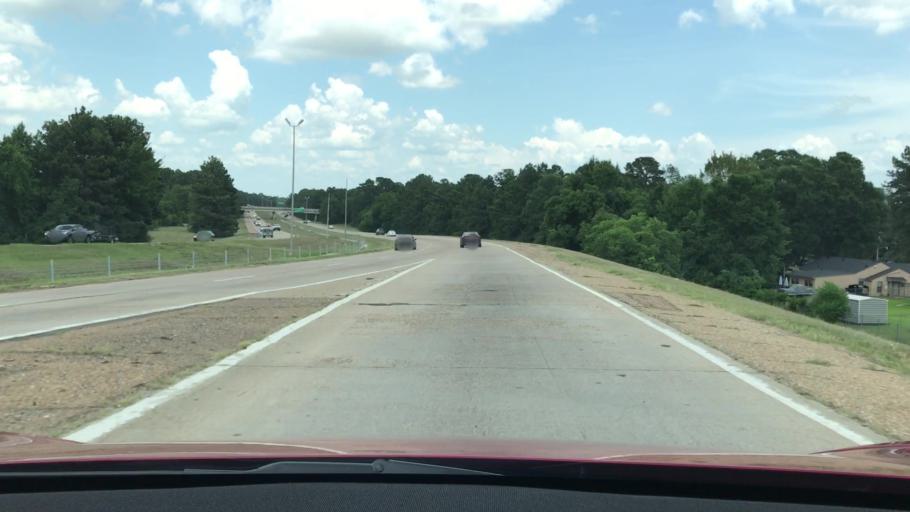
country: US
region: Louisiana
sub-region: Bossier Parish
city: Bossier City
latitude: 32.4153
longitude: -93.7862
